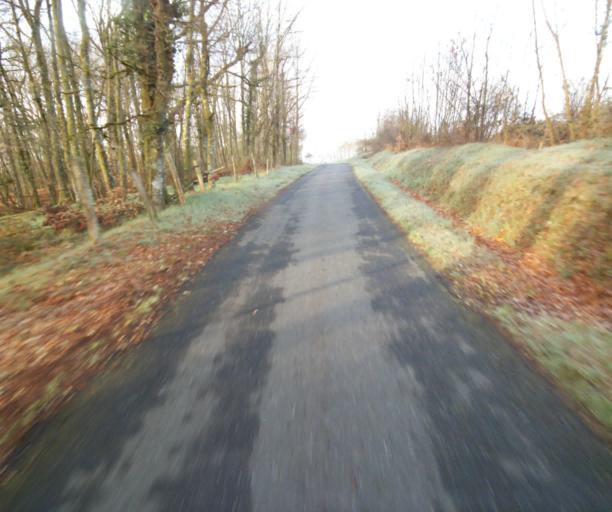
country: FR
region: Limousin
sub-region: Departement de la Correze
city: Correze
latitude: 45.3089
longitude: 1.8561
